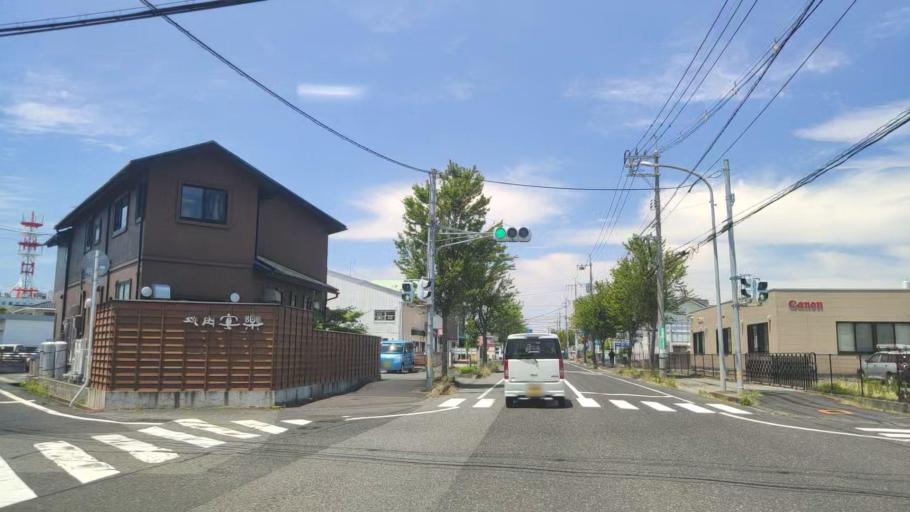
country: JP
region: Tottori
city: Tottori
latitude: 35.4863
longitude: 134.2332
